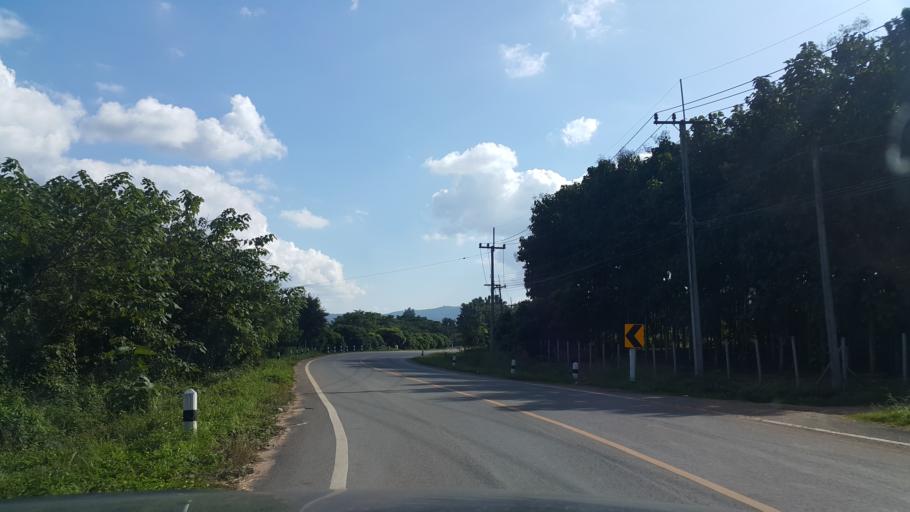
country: TH
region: Lamphun
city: Ban Thi
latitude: 18.5727
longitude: 99.2573
